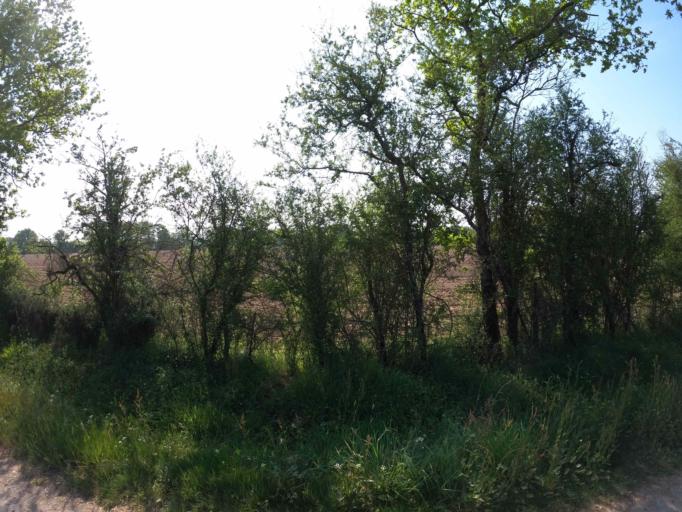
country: FR
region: Pays de la Loire
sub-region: Departement de la Vendee
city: Treize-Septiers
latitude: 47.0016
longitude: -1.2490
